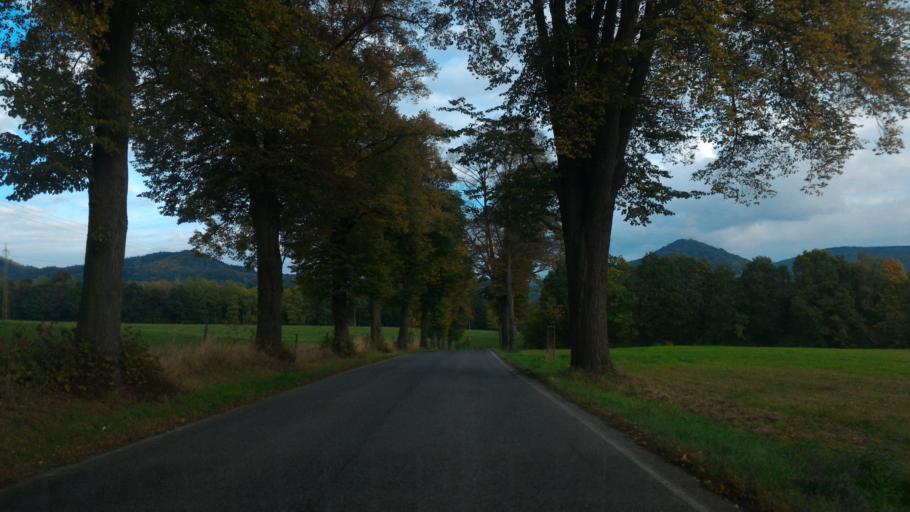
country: CZ
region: Ustecky
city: Ceska Kamenice
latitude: 50.8025
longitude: 14.3951
